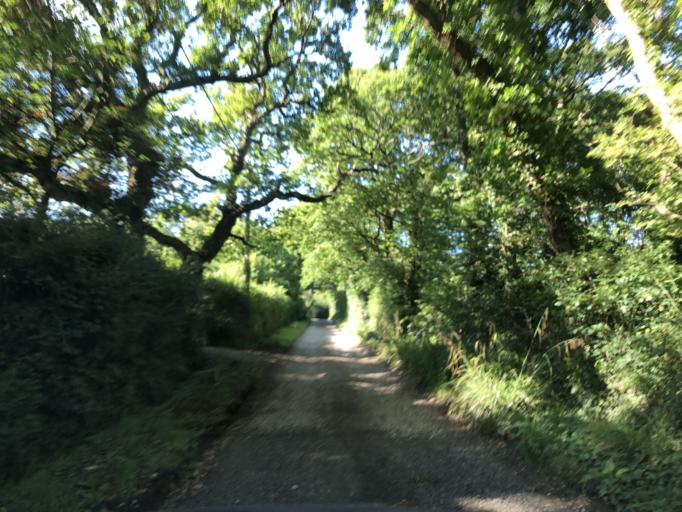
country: GB
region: England
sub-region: Isle of Wight
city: Shalfleet
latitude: 50.7074
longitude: -1.4387
